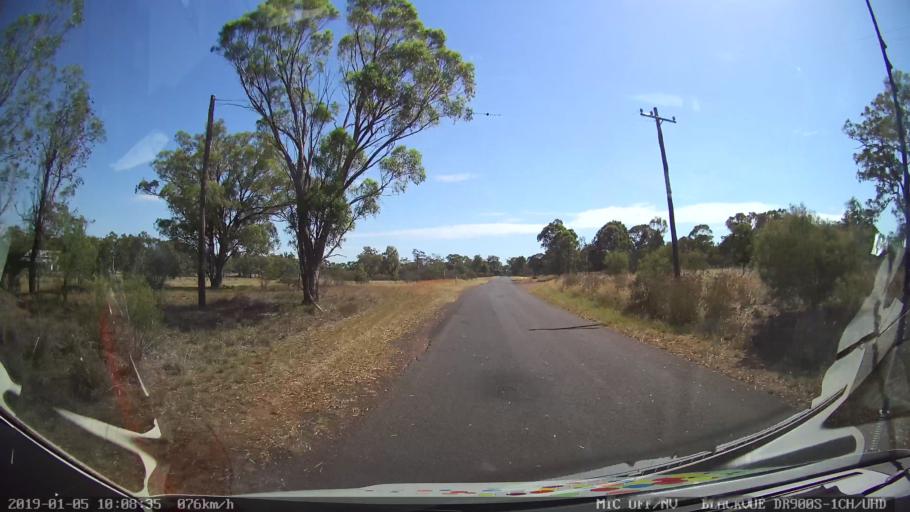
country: AU
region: New South Wales
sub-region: Gilgandra
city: Gilgandra
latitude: -31.6394
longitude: 148.8802
